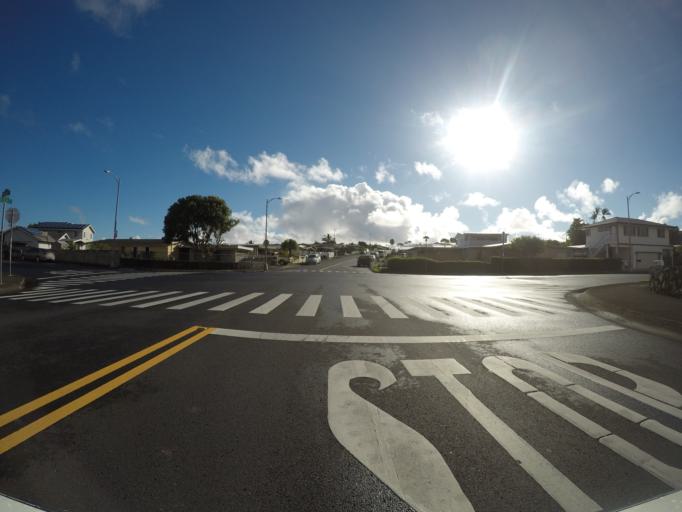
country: US
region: Hawaii
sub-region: Honolulu County
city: He'eia
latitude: 21.4230
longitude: -157.8101
